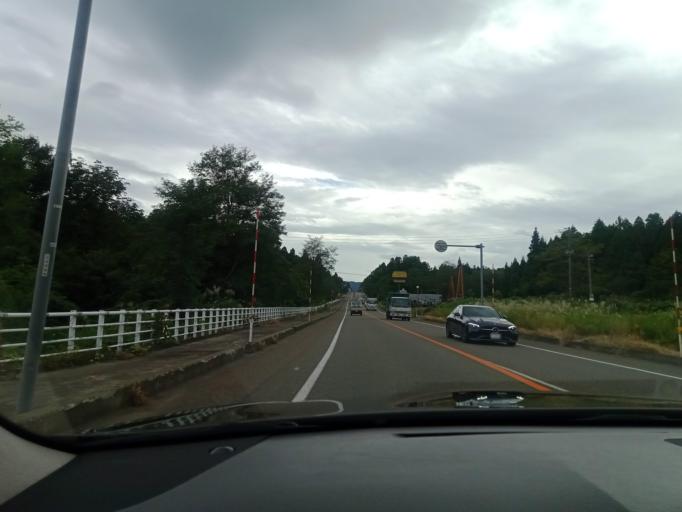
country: JP
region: Niigata
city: Arai
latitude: 36.9532
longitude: 138.2189
